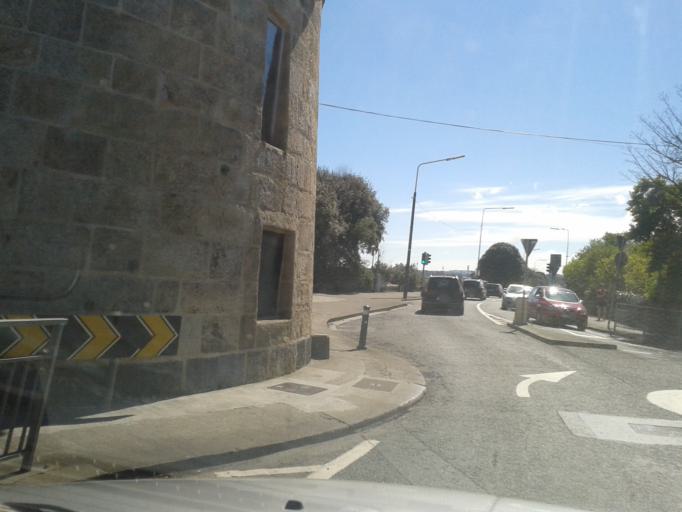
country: IE
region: Leinster
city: Sandymount
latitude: 53.3252
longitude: -6.2071
